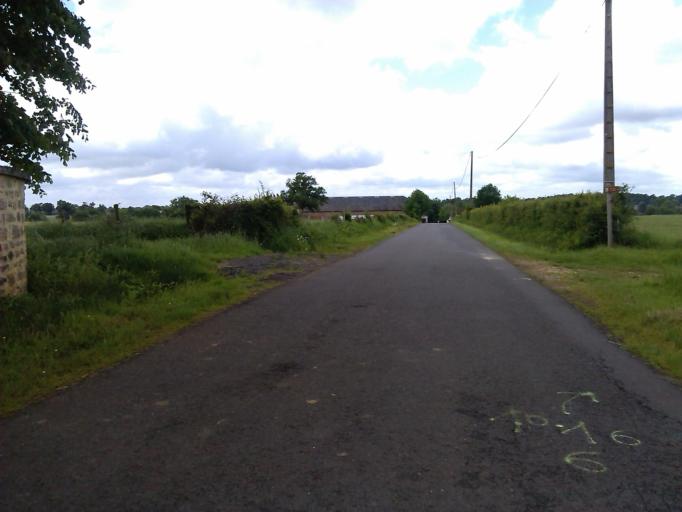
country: FR
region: Poitou-Charentes
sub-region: Departement de la Vienne
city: Availles-Limouzine
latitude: 46.1200
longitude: 0.5803
